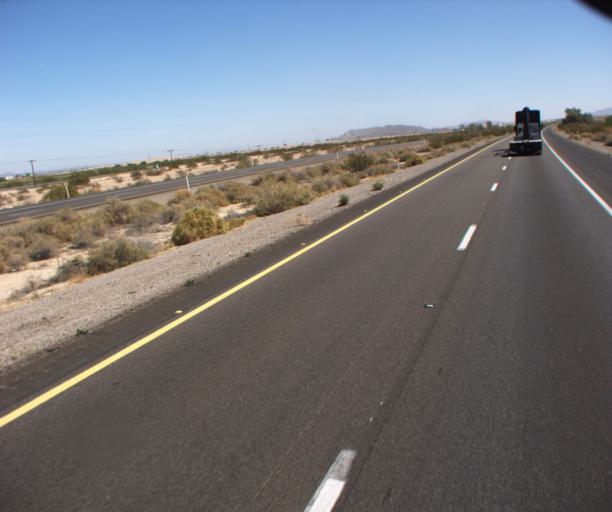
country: US
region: Arizona
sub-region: Yuma County
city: Wellton
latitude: 32.6716
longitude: -114.0998
